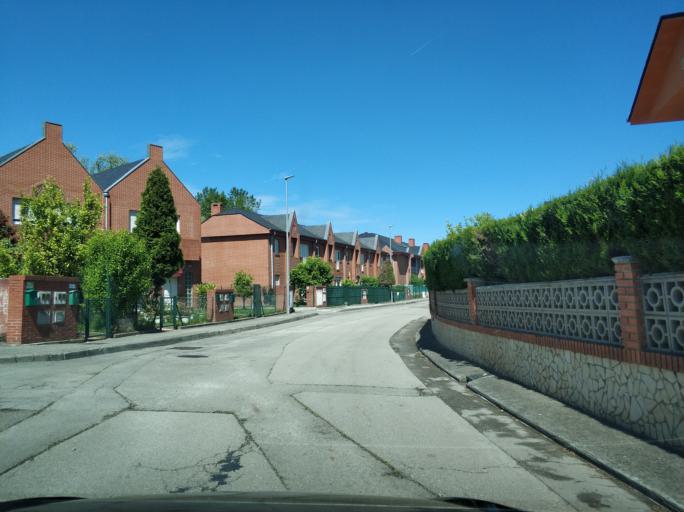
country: ES
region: Cantabria
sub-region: Provincia de Cantabria
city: Puente Viesgo
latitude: 43.3533
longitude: -3.9474
